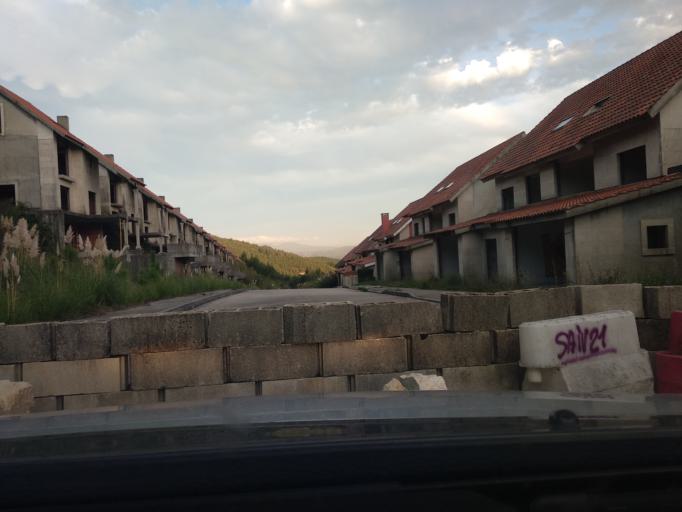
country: ES
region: Galicia
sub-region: Provincia de Pontevedra
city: Moana
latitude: 42.2975
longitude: -8.6900
